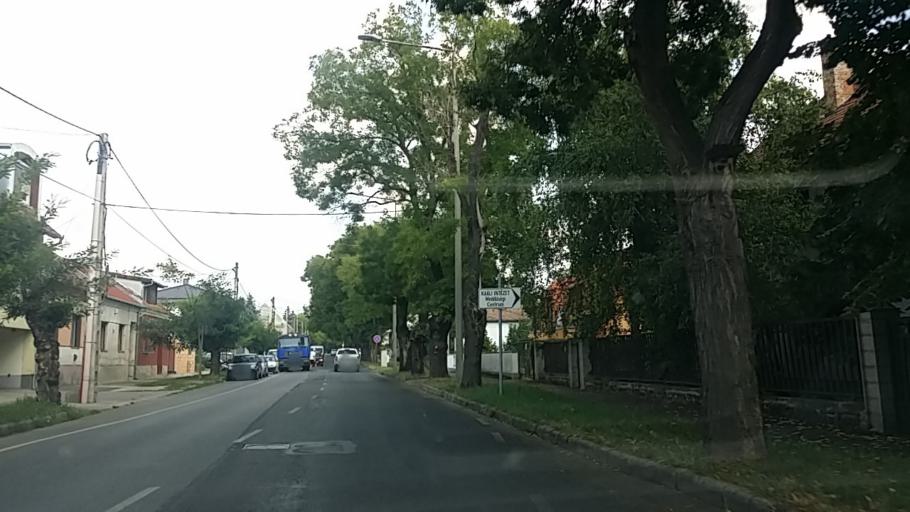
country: HU
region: Baranya
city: Pecs
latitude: 46.0699
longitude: 18.1975
